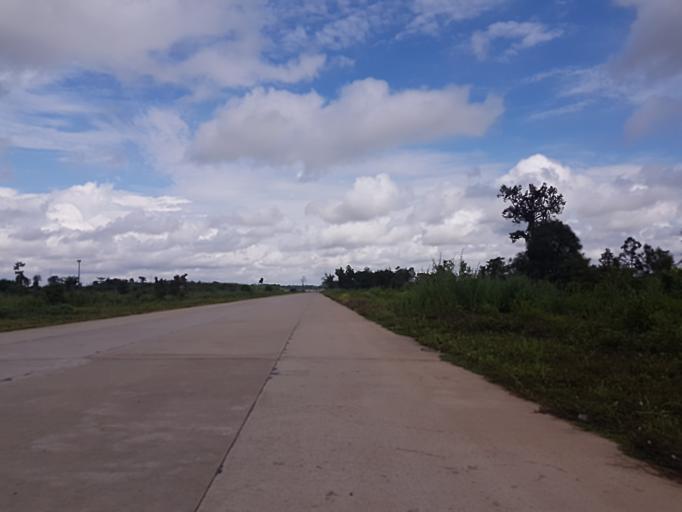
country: TH
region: Nong Khai
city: Nong Khai
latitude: 17.9039
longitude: 102.7102
